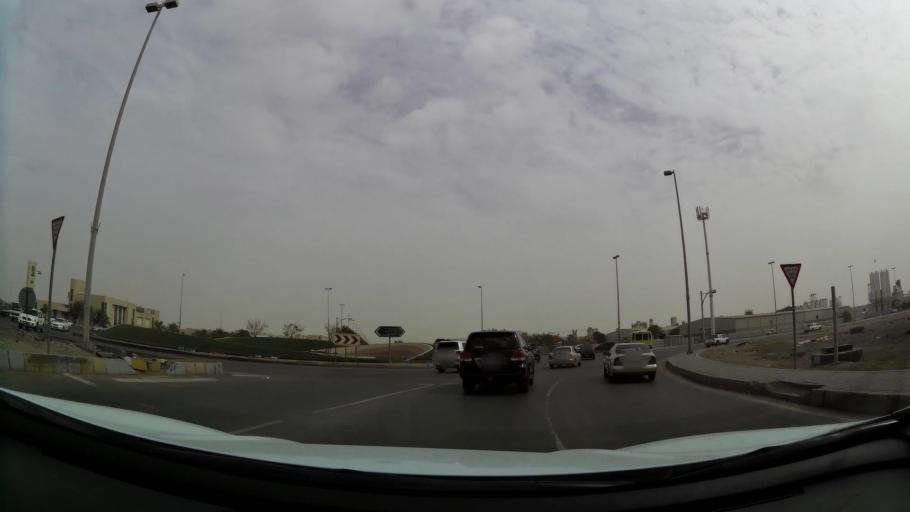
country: AE
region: Abu Dhabi
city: Abu Dhabi
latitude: 24.3457
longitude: 54.5019
